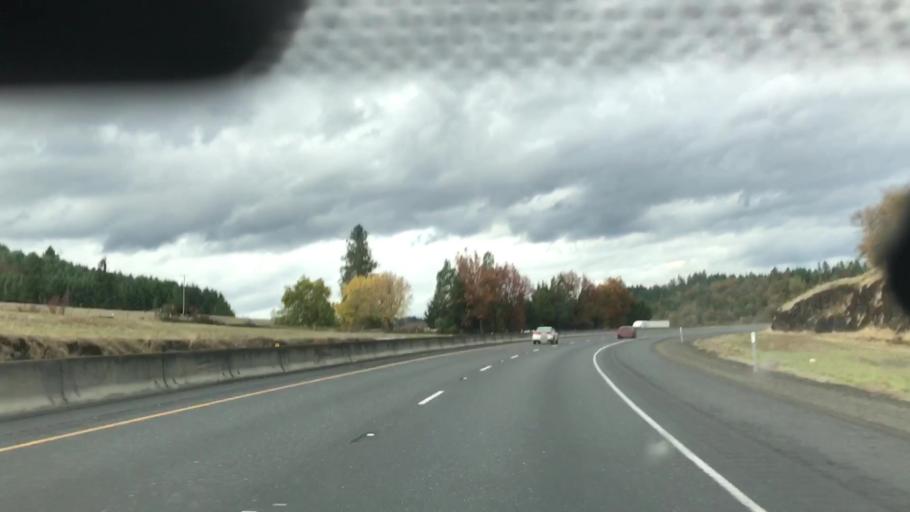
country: US
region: Oregon
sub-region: Douglas County
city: Sutherlin
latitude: 43.4899
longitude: -123.3301
